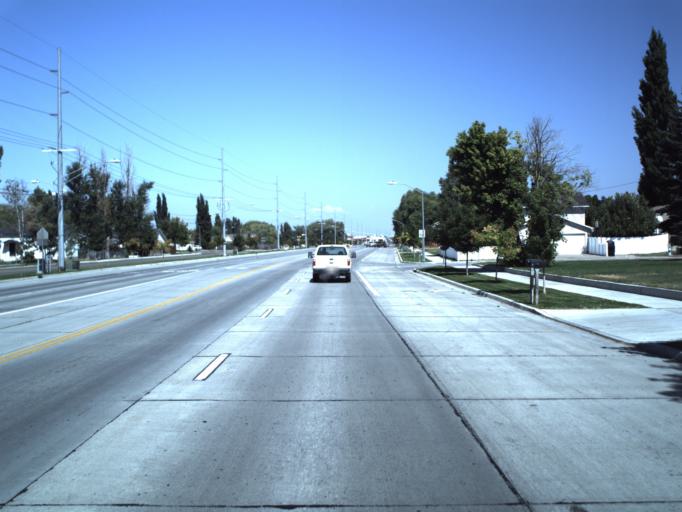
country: US
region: Utah
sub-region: Cache County
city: Logan
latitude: 41.7212
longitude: -111.8599
